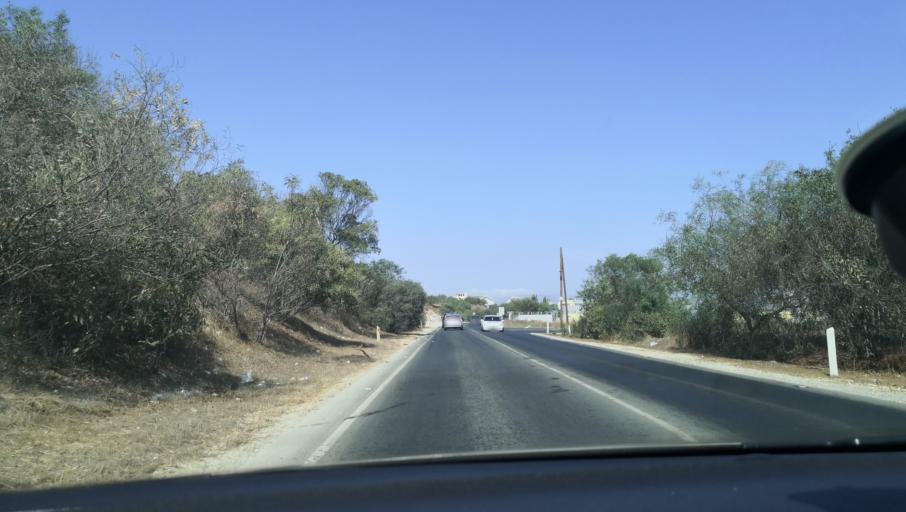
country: CY
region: Lefkosia
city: Kato Deftera
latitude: 35.1089
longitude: 33.2849
